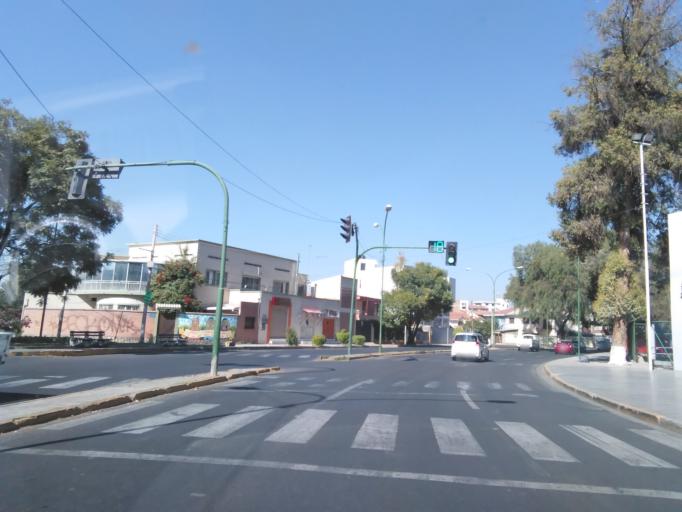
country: BO
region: Cochabamba
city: Cochabamba
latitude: -17.3863
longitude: -66.1625
